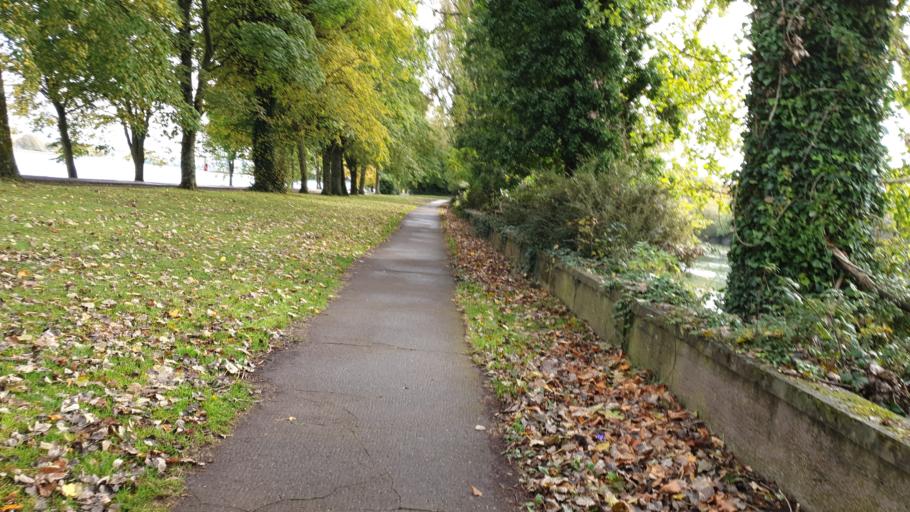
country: IE
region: Munster
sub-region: County Cork
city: Cork
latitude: 51.9003
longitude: -8.4304
